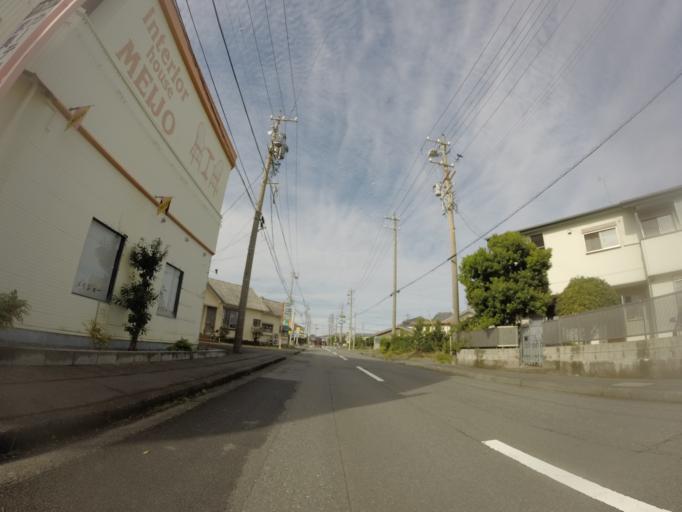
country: JP
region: Shizuoka
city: Shimada
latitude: 34.7684
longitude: 138.2610
